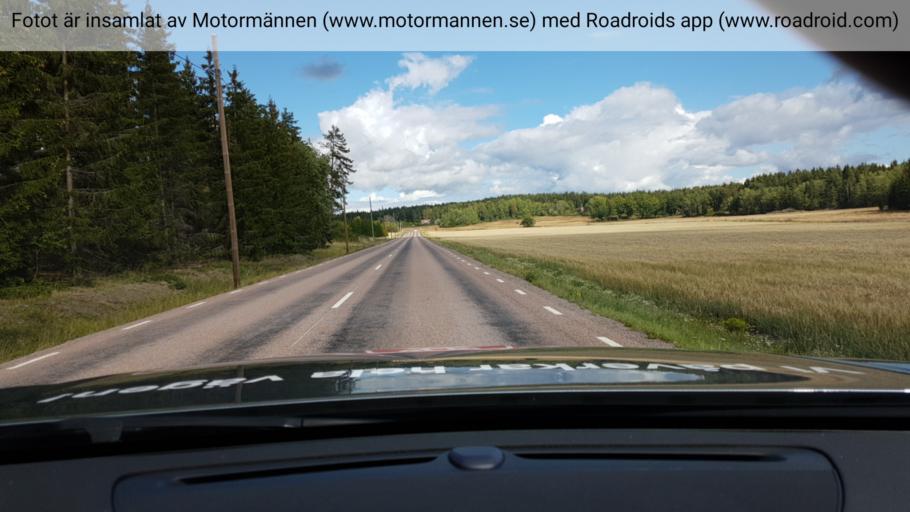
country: SE
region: Soedermanland
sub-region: Strangnas Kommun
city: Mariefred
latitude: 59.2847
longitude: 17.2250
